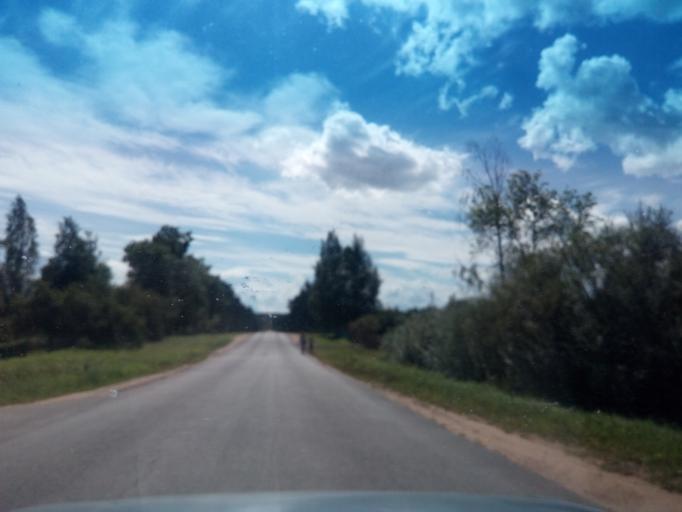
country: BY
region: Vitebsk
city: Dzisna
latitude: 55.6593
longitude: 28.3239
